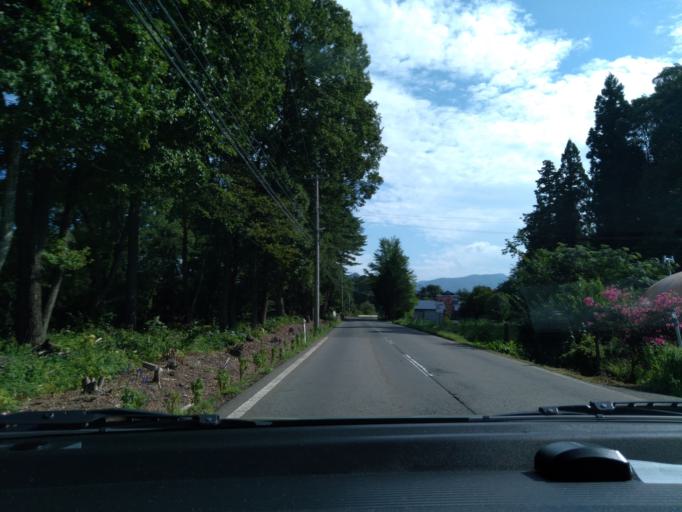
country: JP
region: Iwate
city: Shizukuishi
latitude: 39.6544
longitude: 140.9925
